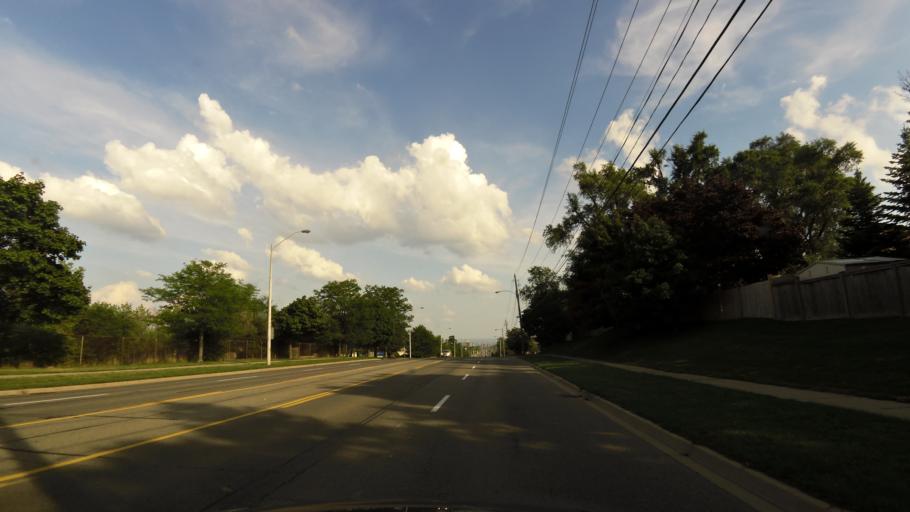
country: CA
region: Ontario
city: Burlington
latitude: 43.3608
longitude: -79.8492
